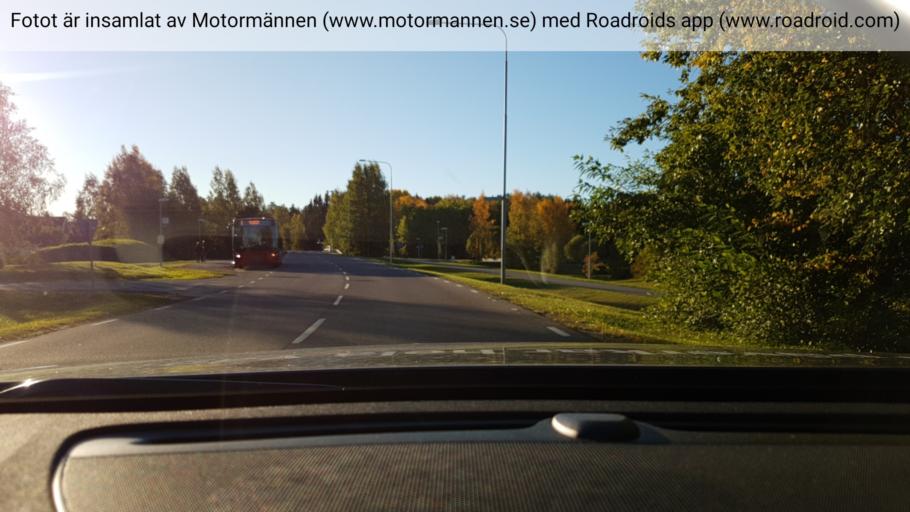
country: SE
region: Norrbotten
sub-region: Lulea Kommun
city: Sodra Sunderbyn
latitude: 65.6545
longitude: 21.9464
